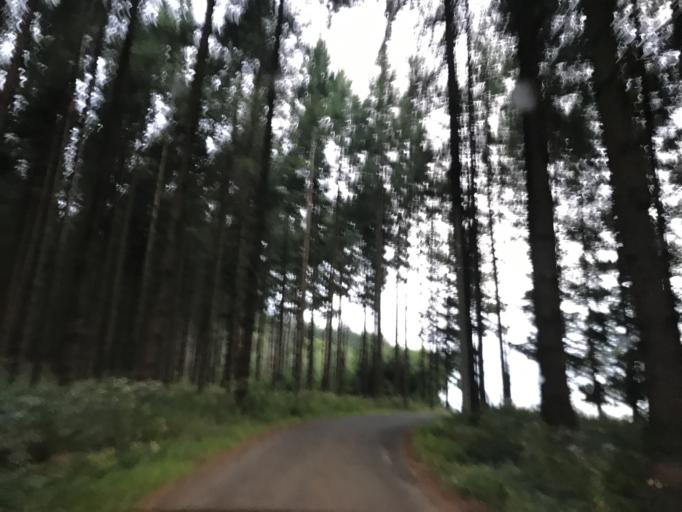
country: FR
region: Auvergne
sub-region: Departement du Puy-de-Dome
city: La Monnerie-le-Montel
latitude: 45.8485
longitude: 3.5982
